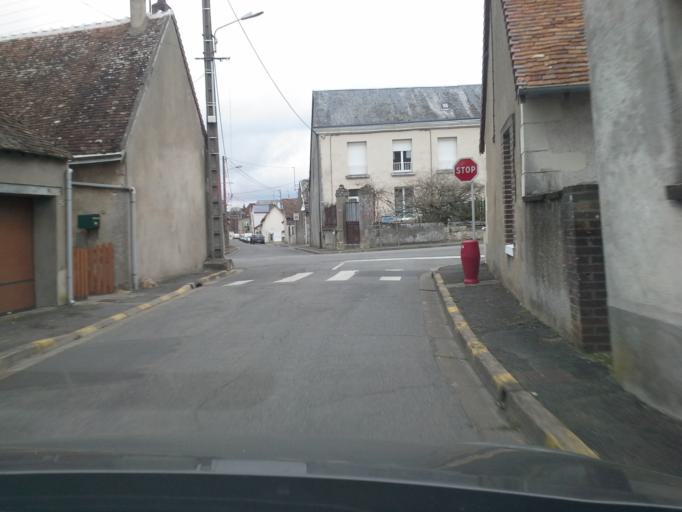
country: FR
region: Centre
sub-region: Departement du Loir-et-Cher
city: Vendome
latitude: 47.7838
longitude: 1.0683
